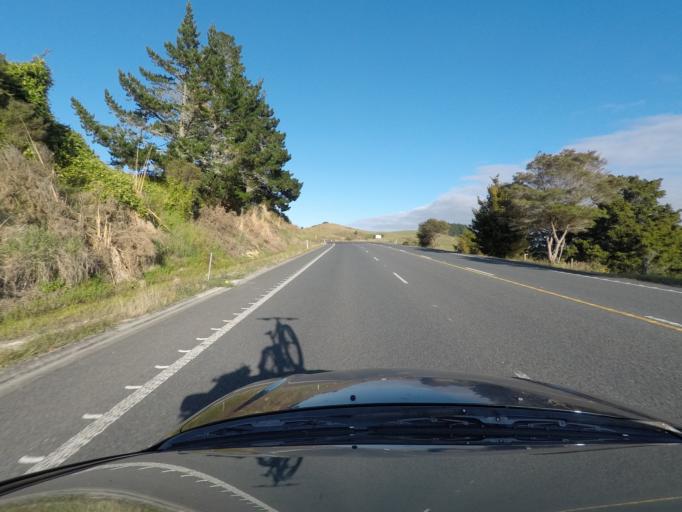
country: NZ
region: Northland
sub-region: Far North District
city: Kawakawa
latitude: -35.4824
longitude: 174.1277
